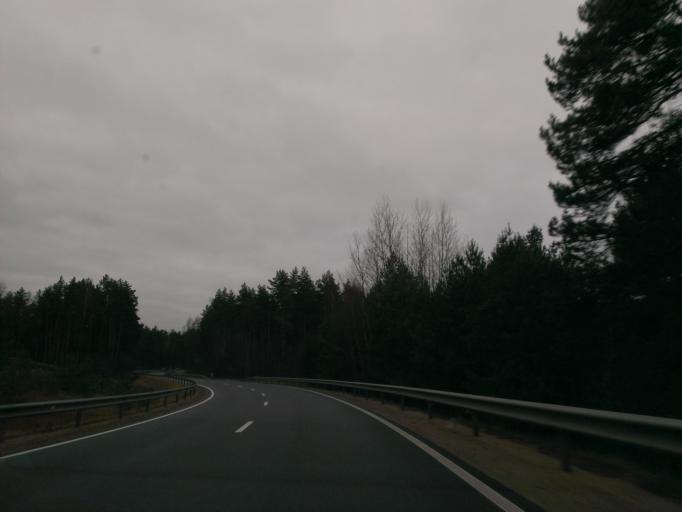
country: LV
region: Riga
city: Bergi
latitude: 57.0113
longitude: 24.3059
